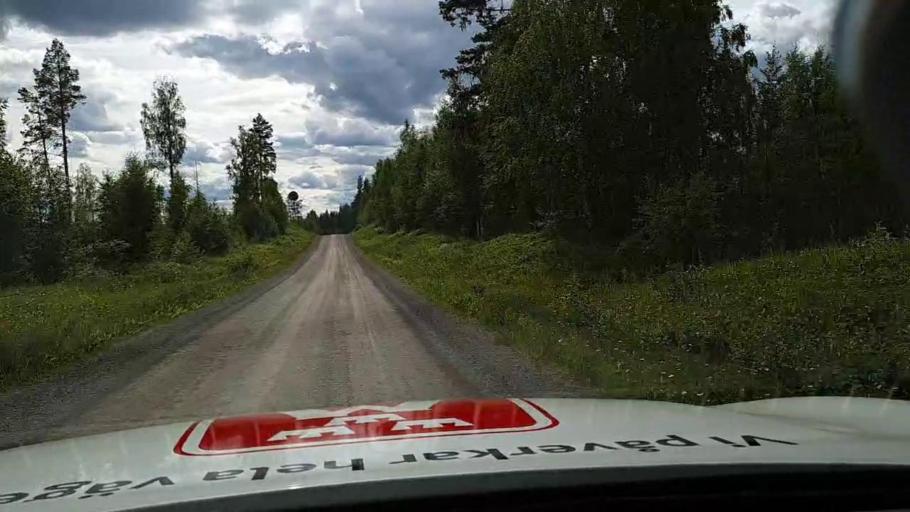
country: SE
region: Jaemtland
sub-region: Braecke Kommun
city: Braecke
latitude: 63.2263
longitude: 15.3490
